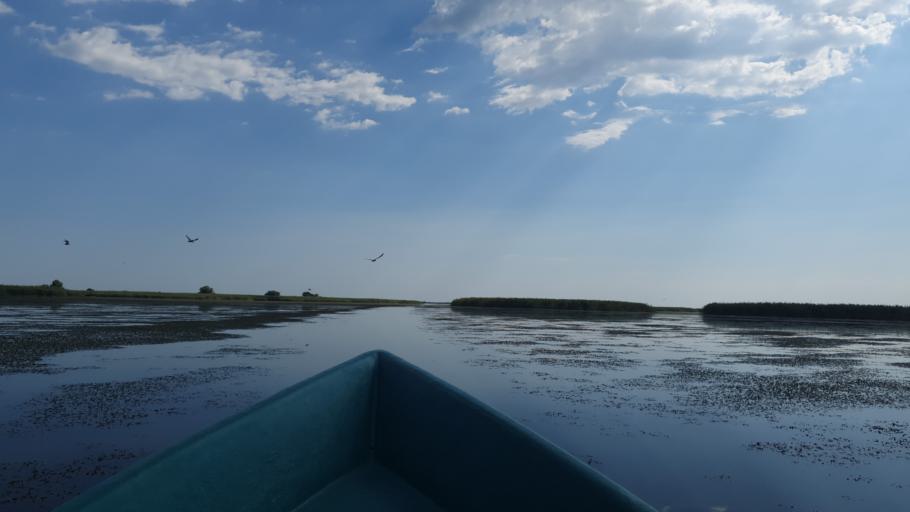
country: RU
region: Astrakhan
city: Kirovskiy
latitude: 45.8404
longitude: 48.4421
